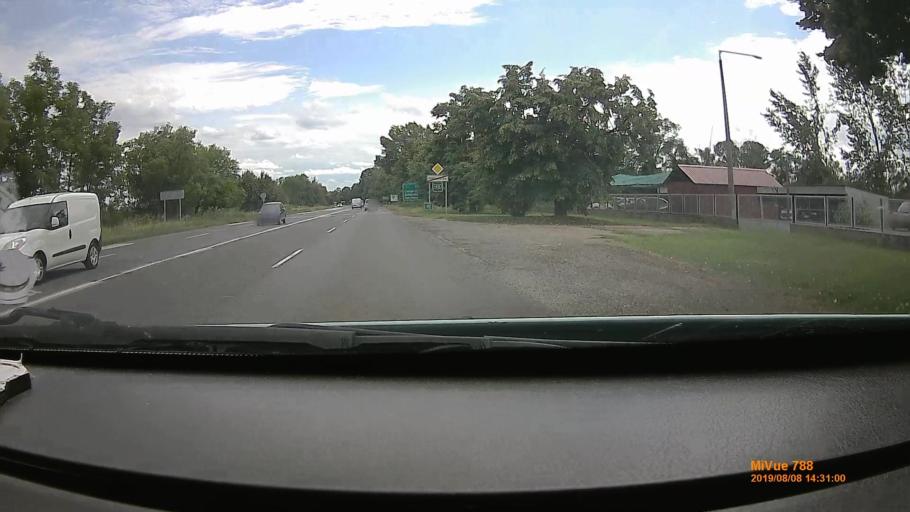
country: HU
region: Szabolcs-Szatmar-Bereg
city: Mateszalka
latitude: 47.9453
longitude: 22.3255
